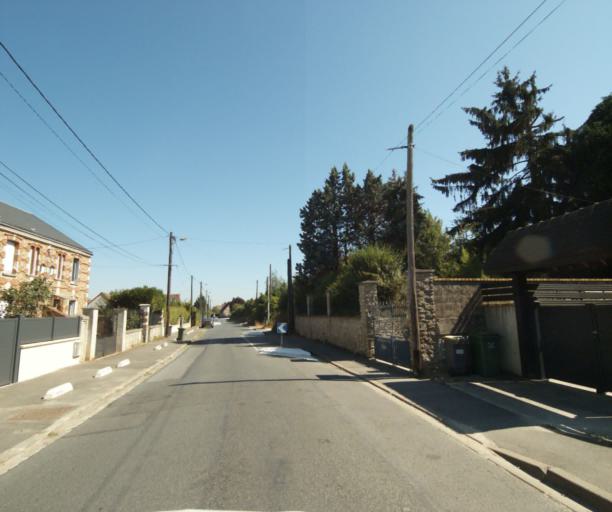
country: FR
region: Ile-de-France
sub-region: Departement de l'Essonne
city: Itteville
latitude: 48.5199
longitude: 2.3485
